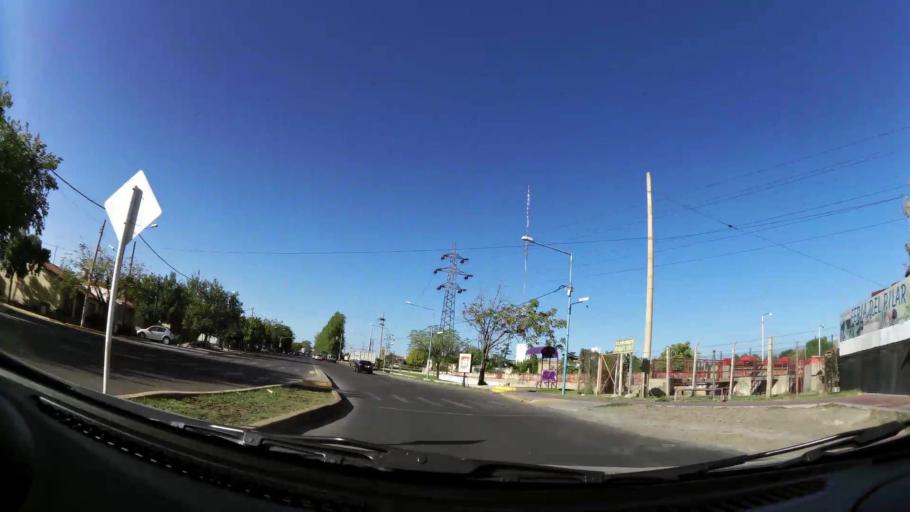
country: AR
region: Mendoza
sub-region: Departamento de Godoy Cruz
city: Godoy Cruz
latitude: -32.9293
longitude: -68.8388
